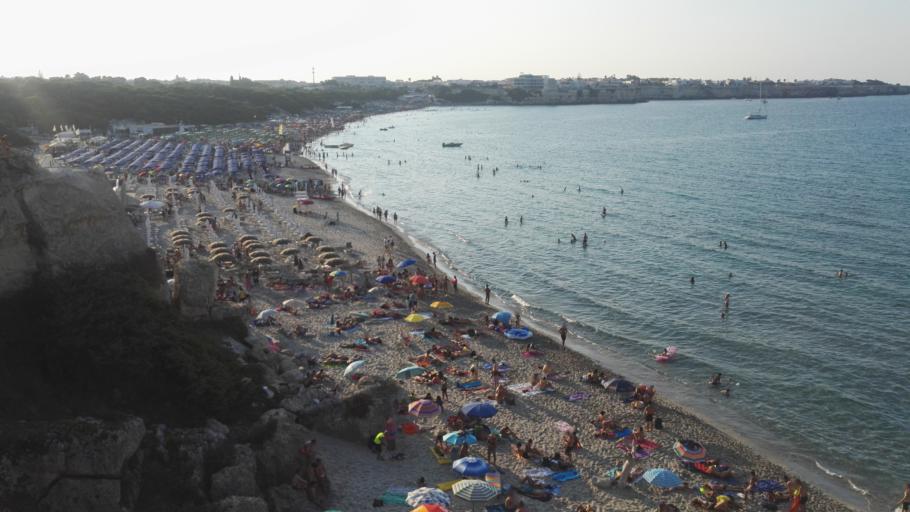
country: IT
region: Apulia
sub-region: Provincia di Lecce
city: Borgagne
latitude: 40.2687
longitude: 18.4353
